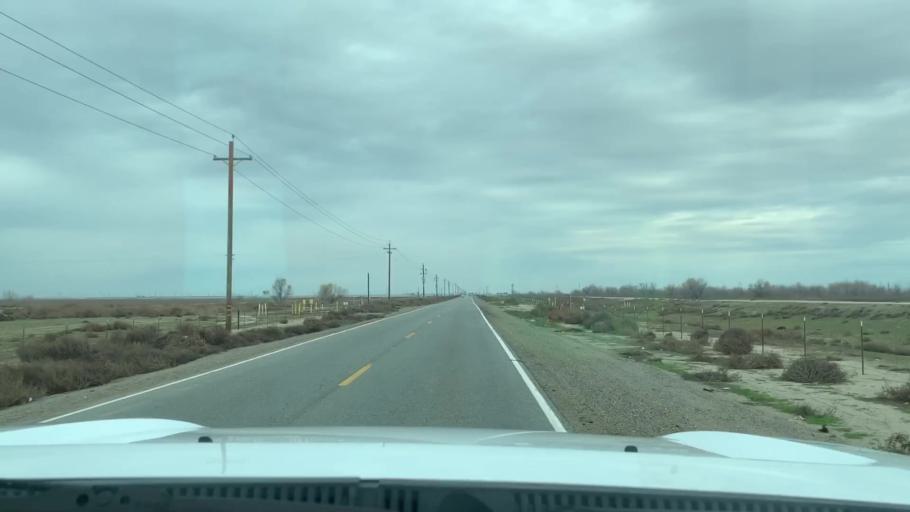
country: US
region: California
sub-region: Kern County
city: Rosedale
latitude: 35.3313
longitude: -119.2524
